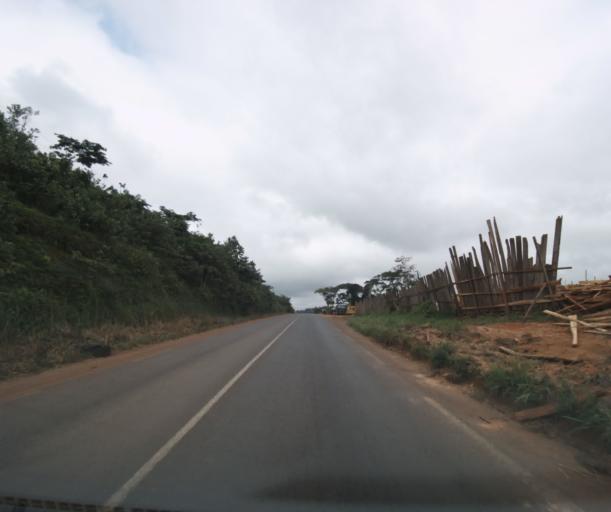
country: CM
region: Centre
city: Mbankomo
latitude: 3.7845
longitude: 11.4620
